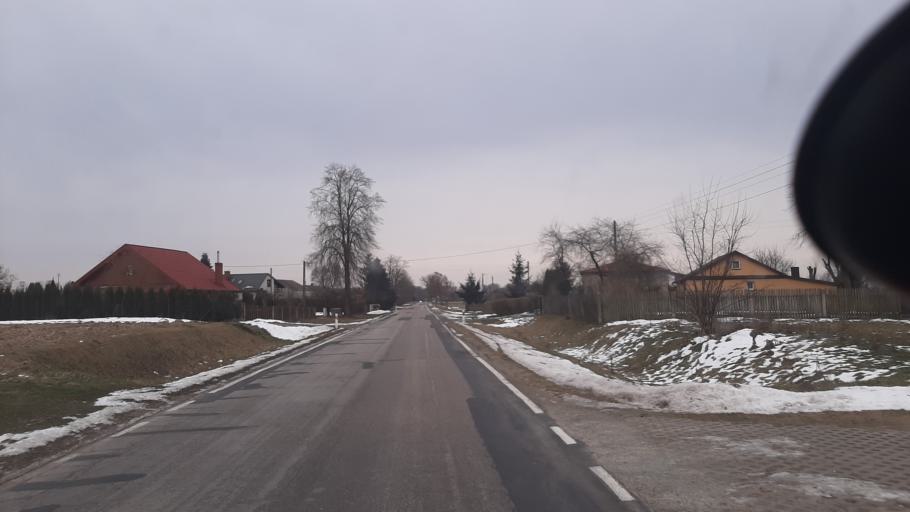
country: PL
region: Lublin Voivodeship
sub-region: Powiat lubartowski
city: Kamionka
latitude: 51.4563
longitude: 22.4209
